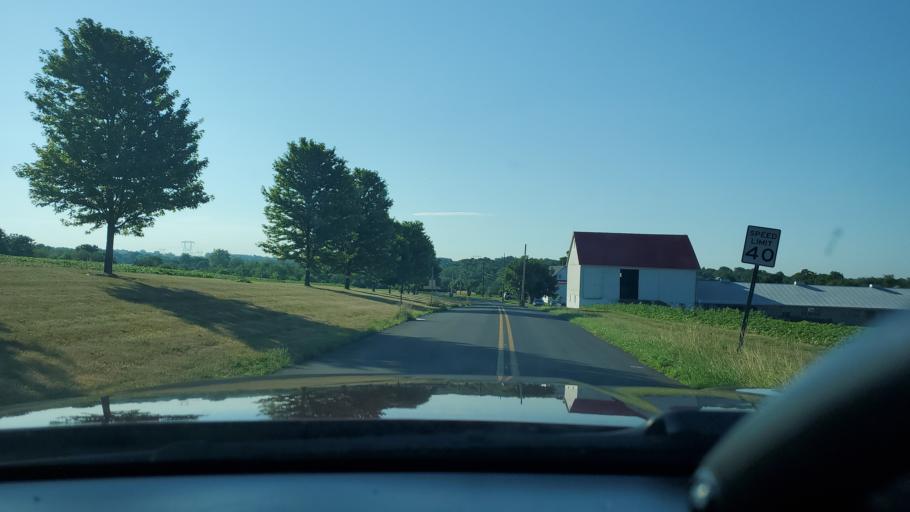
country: US
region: Pennsylvania
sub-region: Montgomery County
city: Harleysville
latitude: 40.3019
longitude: -75.4064
